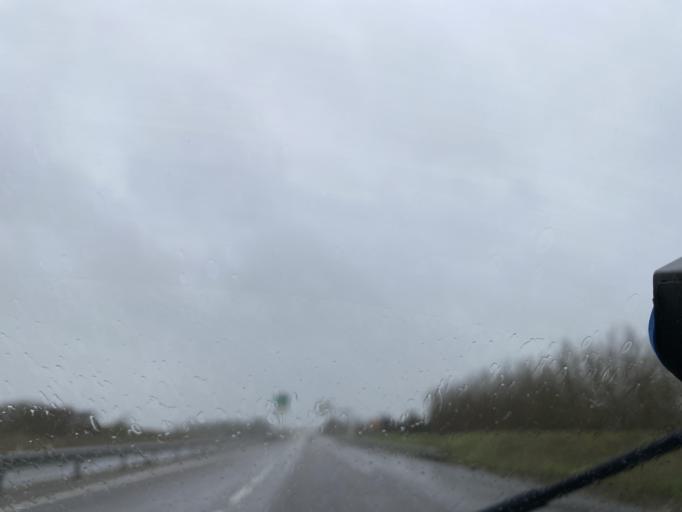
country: FR
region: Haute-Normandie
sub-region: Departement de l'Eure
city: Damville
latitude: 48.8924
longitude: 1.1717
